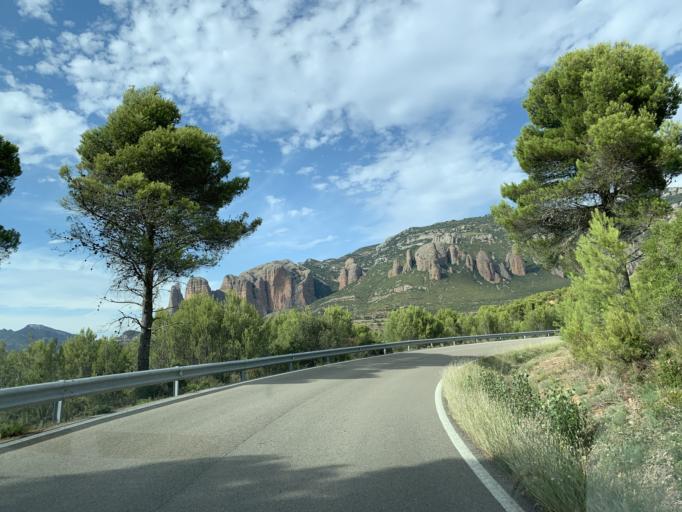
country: ES
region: Aragon
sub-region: Provincia de Zaragoza
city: Santa Eulalia de Gallego
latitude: 42.3295
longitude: -0.7235
